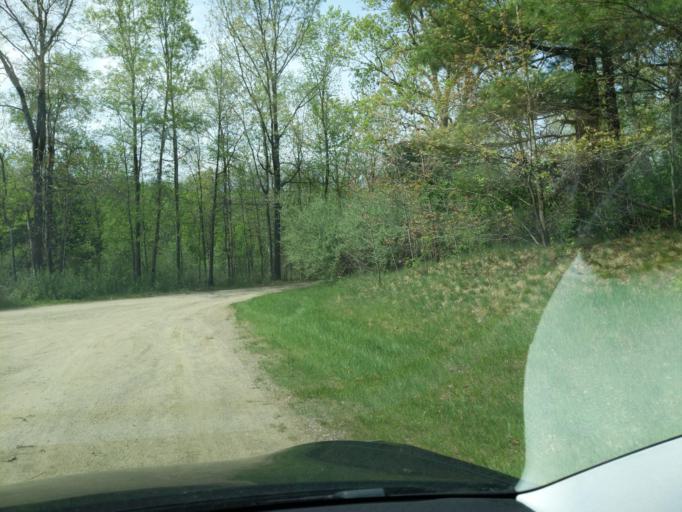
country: US
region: Michigan
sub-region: Washtenaw County
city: Chelsea
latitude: 42.4047
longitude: -84.0581
